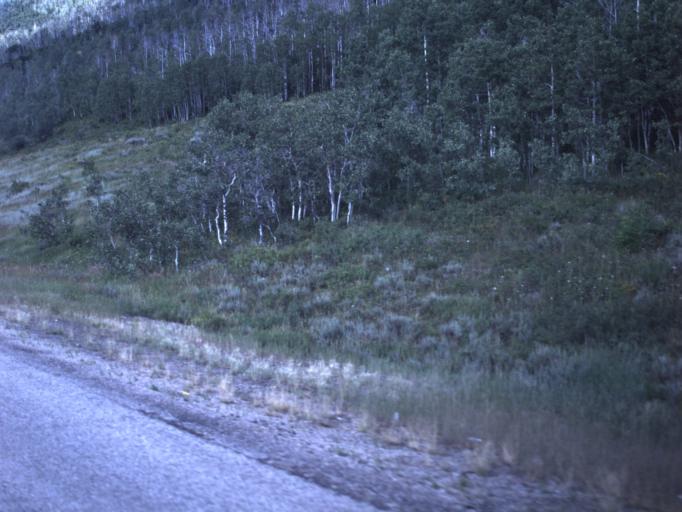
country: US
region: Utah
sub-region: Wasatch County
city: Heber
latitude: 40.3167
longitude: -111.2580
